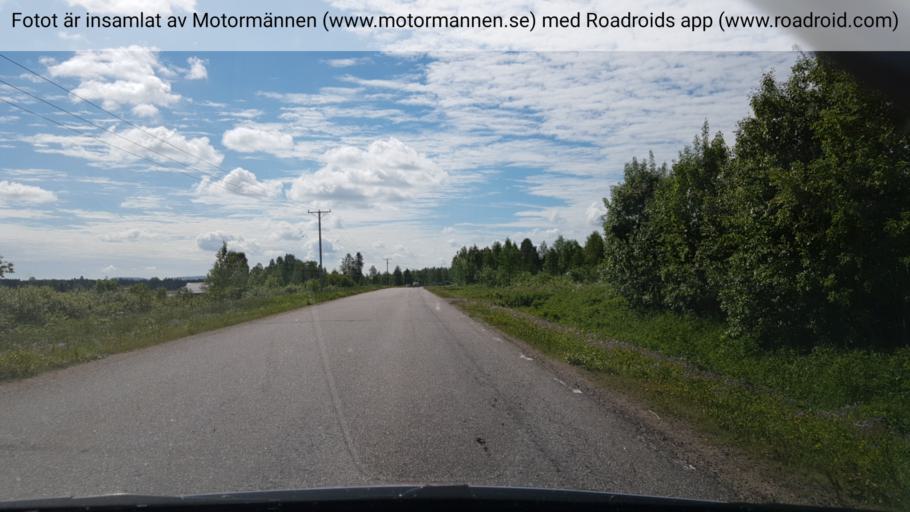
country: FI
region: Lapland
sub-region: Torniolaakso
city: Pello
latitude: 66.6457
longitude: 23.8640
